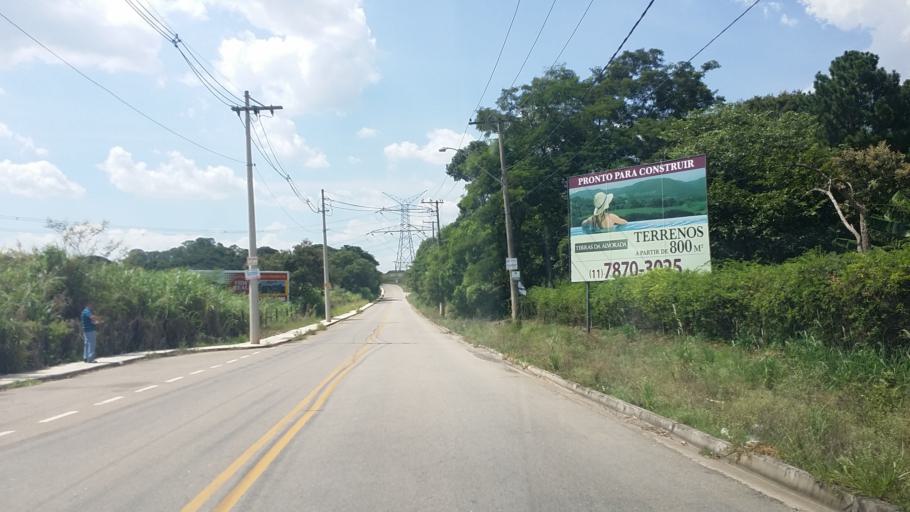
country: BR
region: Sao Paulo
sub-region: Itupeva
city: Itupeva
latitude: -23.2137
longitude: -47.0184
